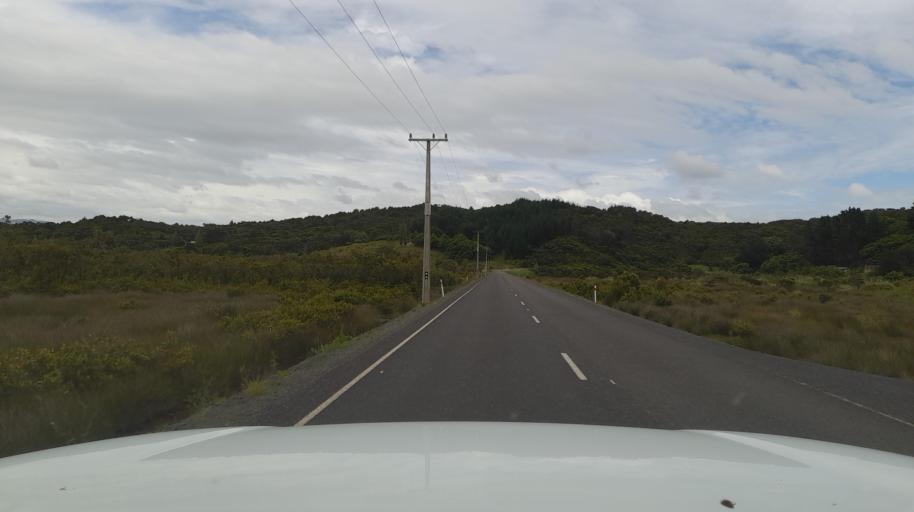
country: NZ
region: Northland
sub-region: Far North District
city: Kaitaia
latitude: -35.4041
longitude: 173.3822
